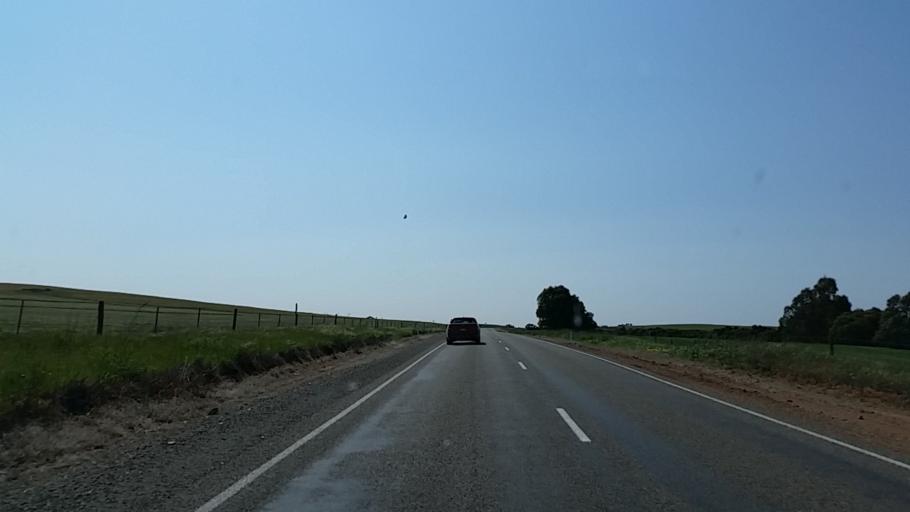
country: AU
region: South Australia
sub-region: Northern Areas
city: Jamestown
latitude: -33.2070
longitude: 138.4326
